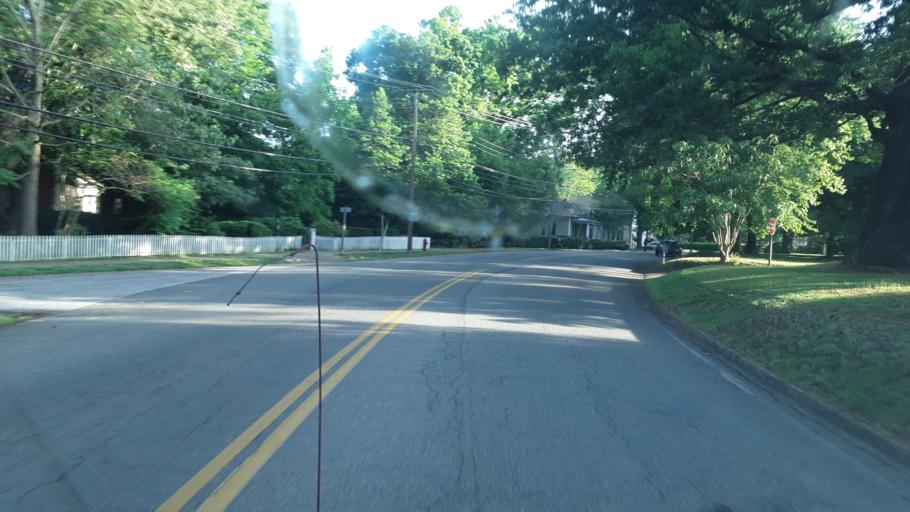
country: US
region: Virginia
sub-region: Pittsylvania County
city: Chatham
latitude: 36.8306
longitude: -79.3969
